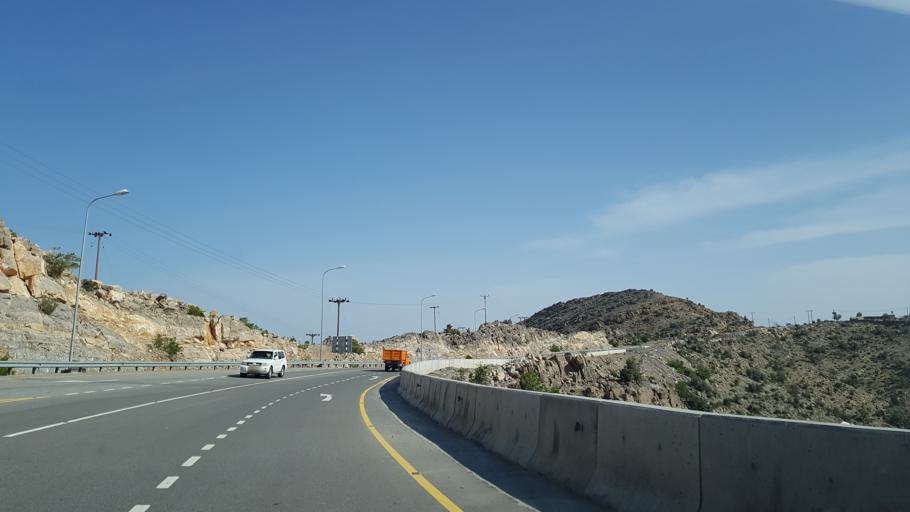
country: OM
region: Muhafazat ad Dakhiliyah
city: Izki
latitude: 23.0586
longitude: 57.7278
